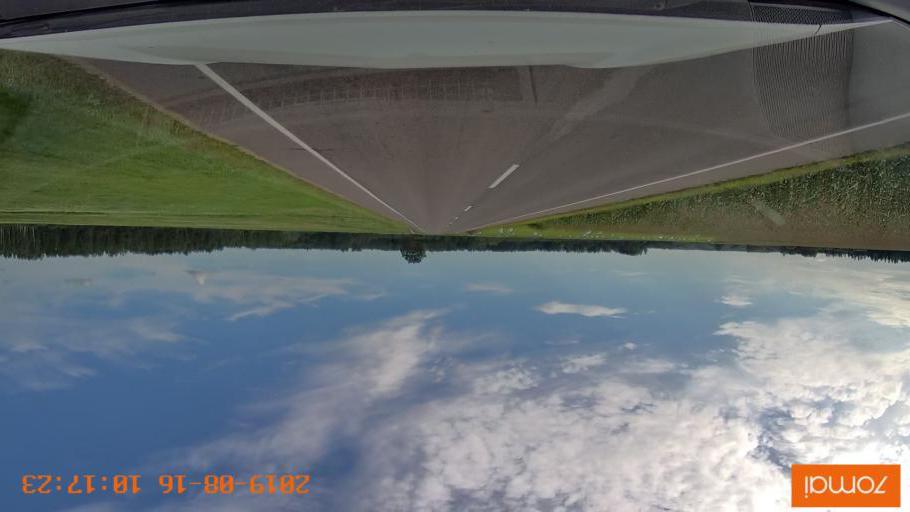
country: BY
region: Mogilev
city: Asipovichy
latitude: 53.3114
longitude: 28.7121
